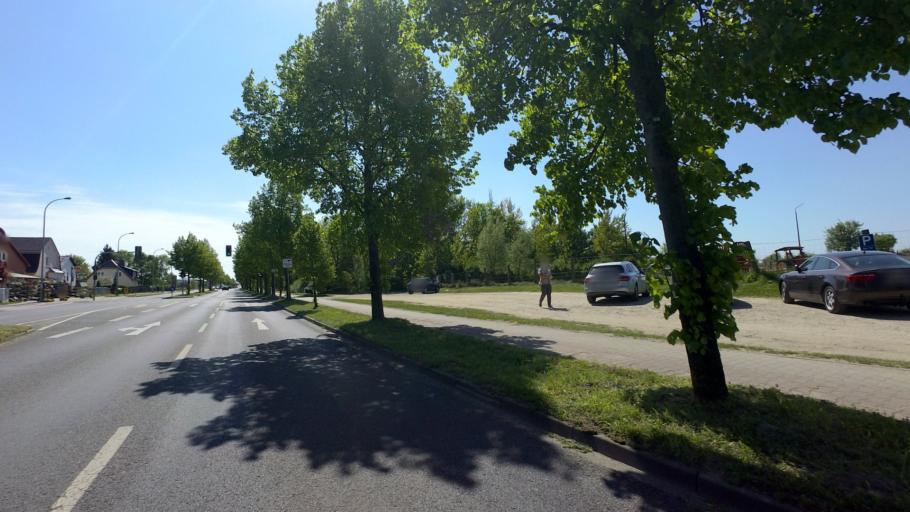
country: DE
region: Brandenburg
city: Schonefeld
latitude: 52.4010
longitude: 13.5141
